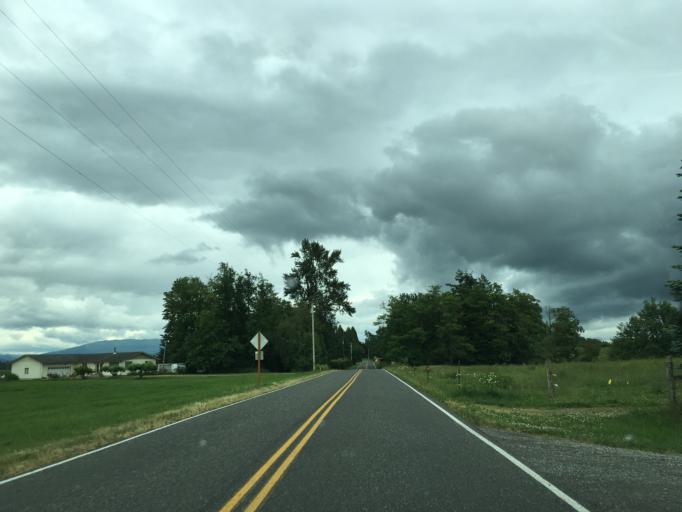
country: US
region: Washington
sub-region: Whatcom County
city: Everson
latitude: 48.9815
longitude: -122.3850
